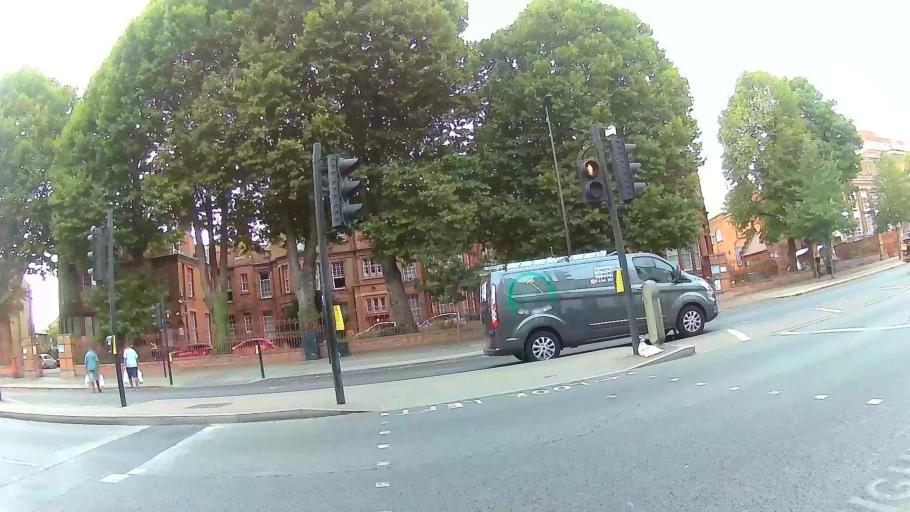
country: GB
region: England
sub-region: Greater London
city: Harringay
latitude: 51.5854
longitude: -0.0716
